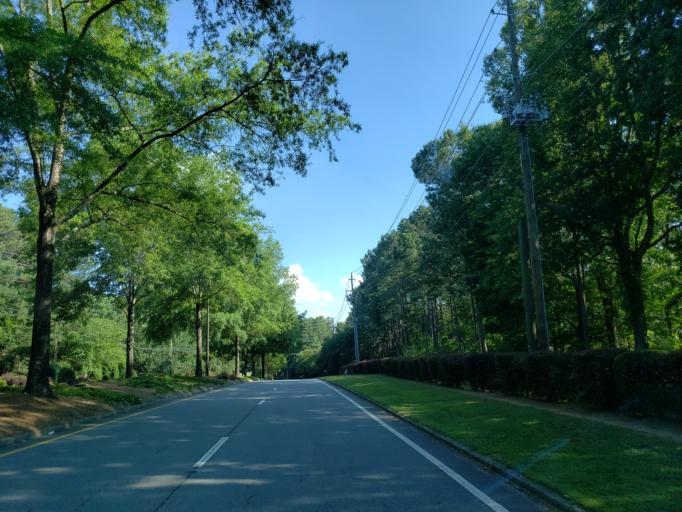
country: US
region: Georgia
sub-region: Cherokee County
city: Woodstock
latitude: 34.1291
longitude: -84.5600
